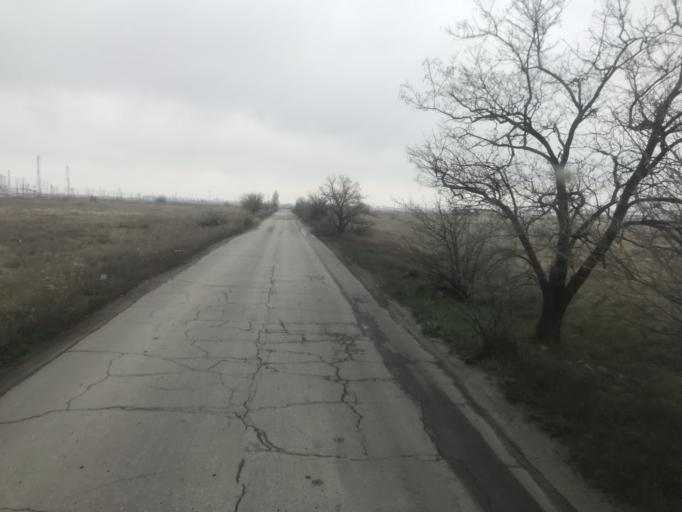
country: RU
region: Volgograd
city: Svetlyy Yar
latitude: 48.4995
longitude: 44.6472
